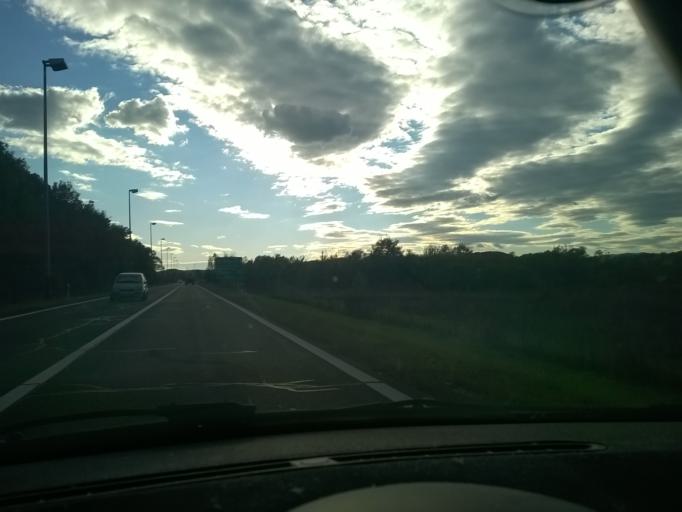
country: HR
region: Krapinsko-Zagorska
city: Oroslavje
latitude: 46.0008
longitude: 15.8716
